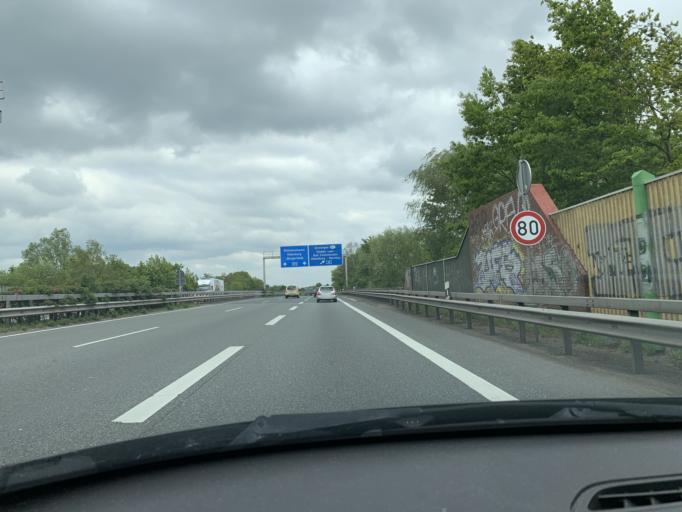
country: DE
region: Lower Saxony
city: Oldenburg
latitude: 53.1486
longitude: 8.1934
